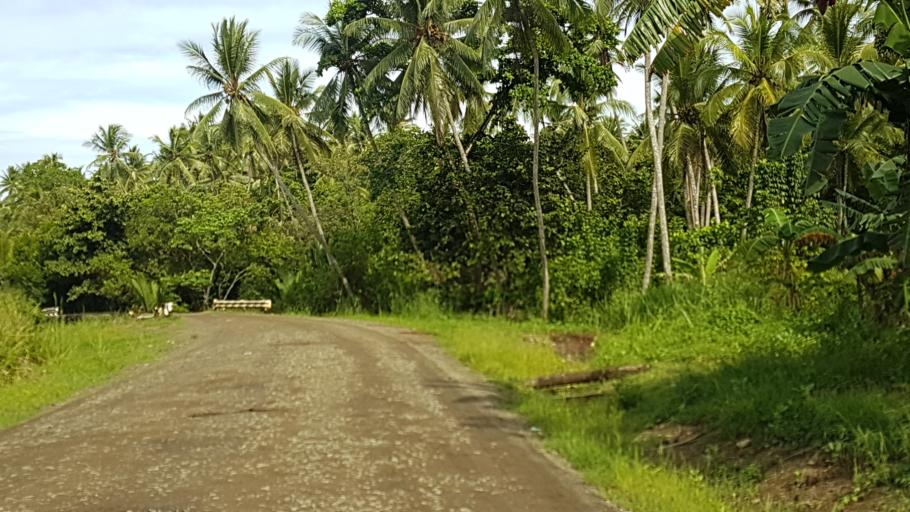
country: PG
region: Milne Bay
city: Alotau
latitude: -10.3328
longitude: 150.6511
